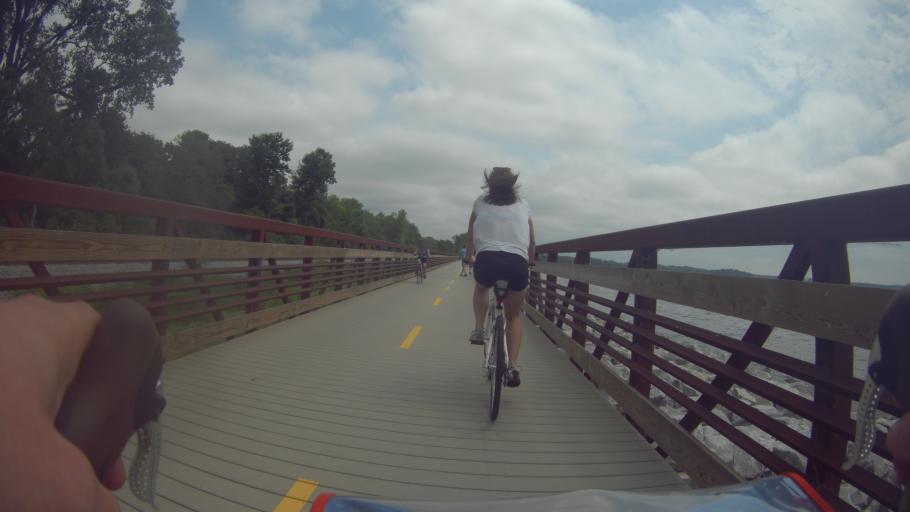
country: US
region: Wisconsin
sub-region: Dane County
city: McFarland
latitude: 43.0319
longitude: -89.3169
